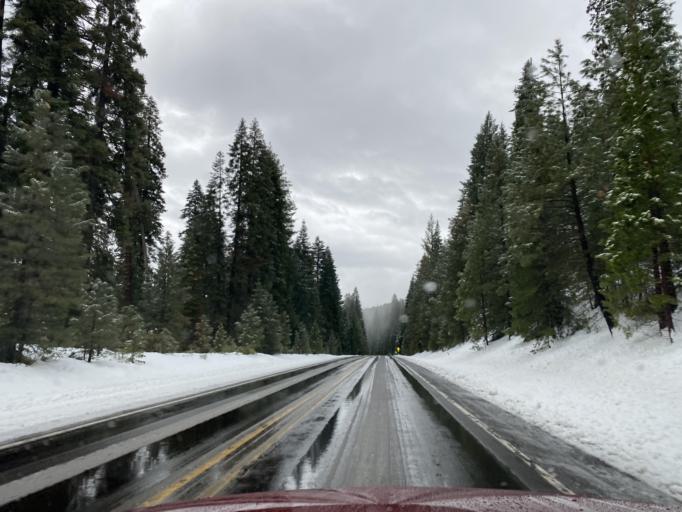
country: US
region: Oregon
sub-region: Klamath County
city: Klamath Falls
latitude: 42.5300
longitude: -122.0897
